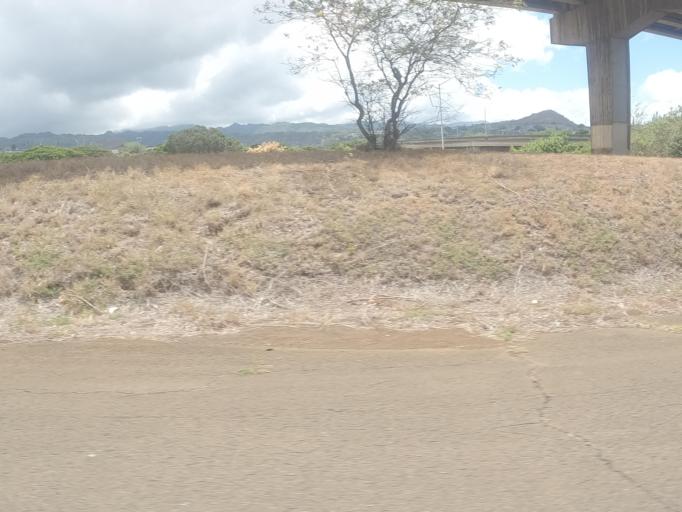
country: US
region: Hawaii
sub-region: Honolulu County
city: Halawa
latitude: 21.3723
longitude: -157.9273
